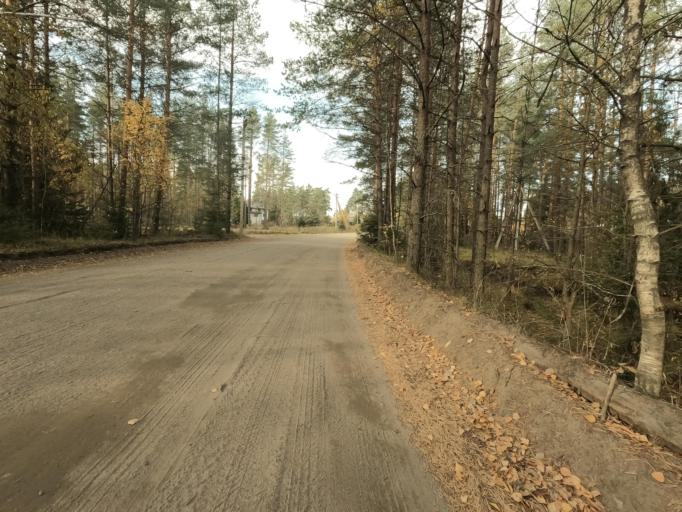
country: RU
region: Leningrad
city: Priladozhskiy
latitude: 59.6320
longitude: 31.3891
